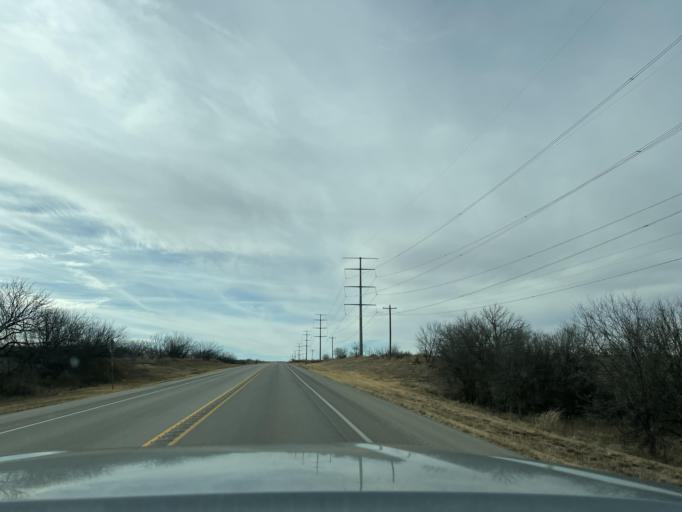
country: US
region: Texas
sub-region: Jones County
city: Stamford
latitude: 32.7503
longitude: -99.6347
